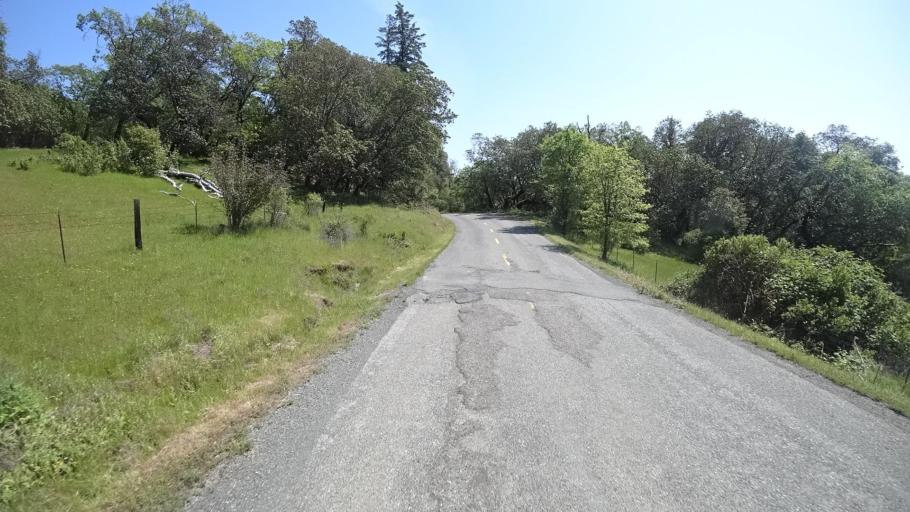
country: US
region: California
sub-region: Humboldt County
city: Redway
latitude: 40.2586
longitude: -123.6253
